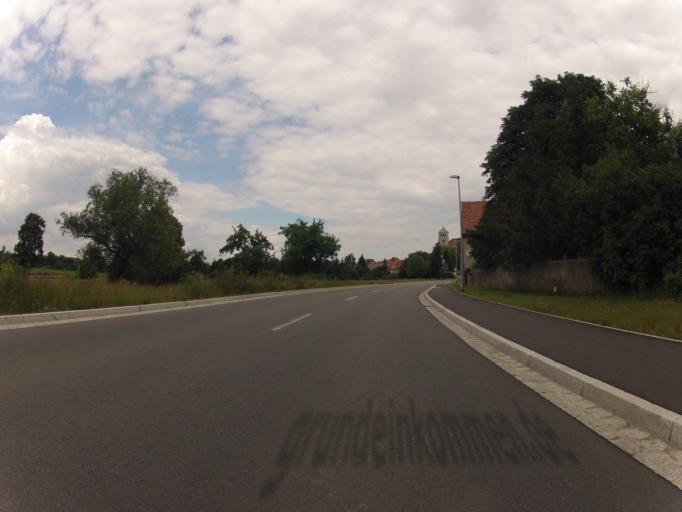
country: DE
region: Saxony
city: Schildau
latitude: 51.4514
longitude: 12.9299
